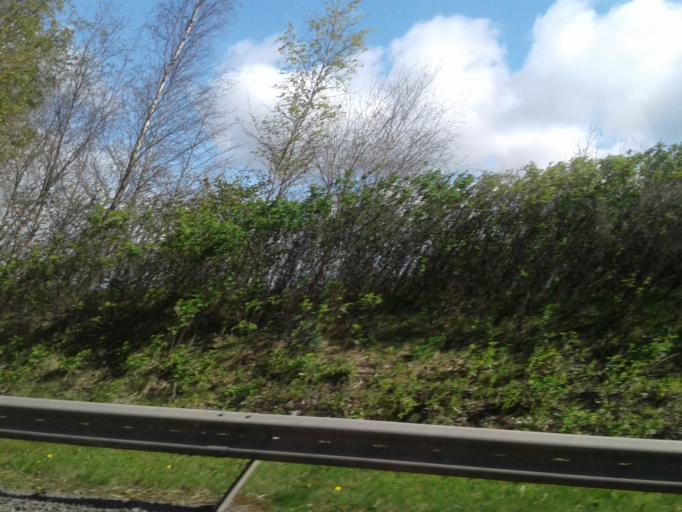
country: IE
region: Leinster
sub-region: An Mhi
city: Ashbourne
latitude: 53.4679
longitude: -6.3620
